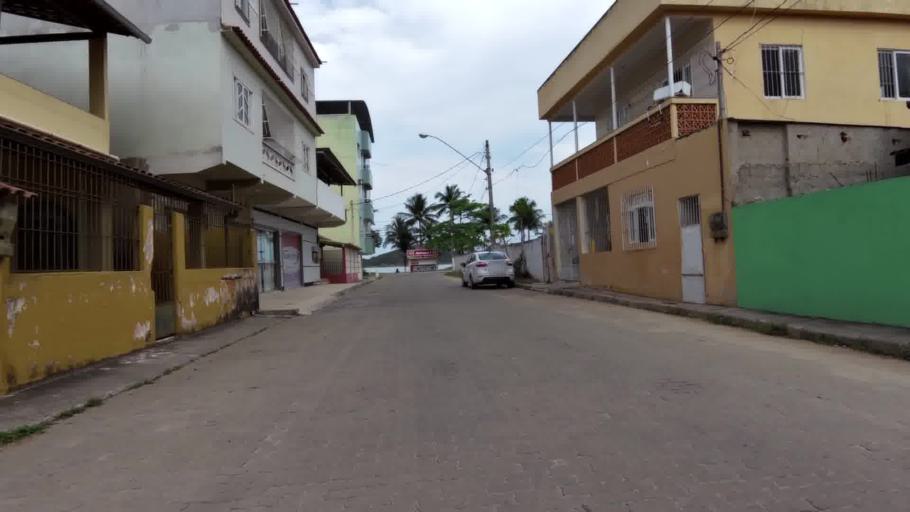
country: BR
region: Espirito Santo
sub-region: Piuma
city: Piuma
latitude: -20.8412
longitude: -40.7284
